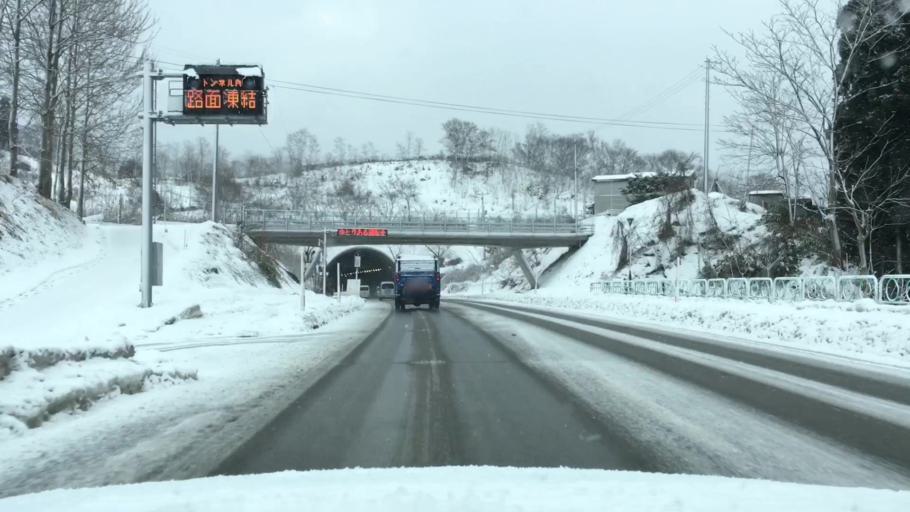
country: JP
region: Aomori
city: Hirosaki
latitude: 40.5253
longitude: 140.5610
